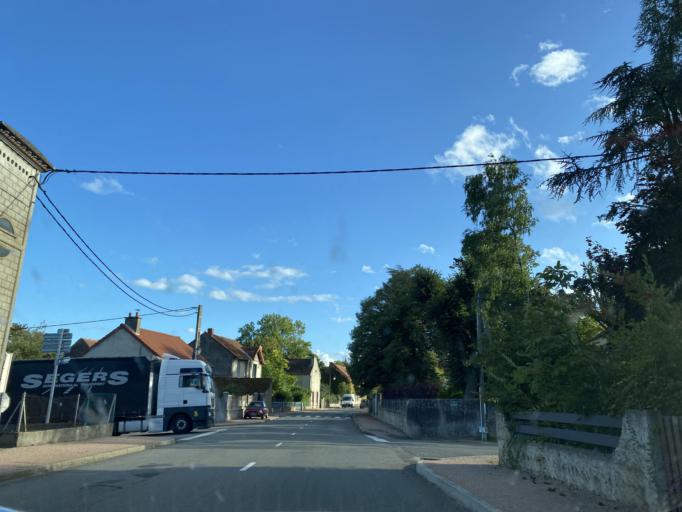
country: FR
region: Auvergne
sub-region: Departement de l'Allier
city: Gannat
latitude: 46.0807
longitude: 3.2706
